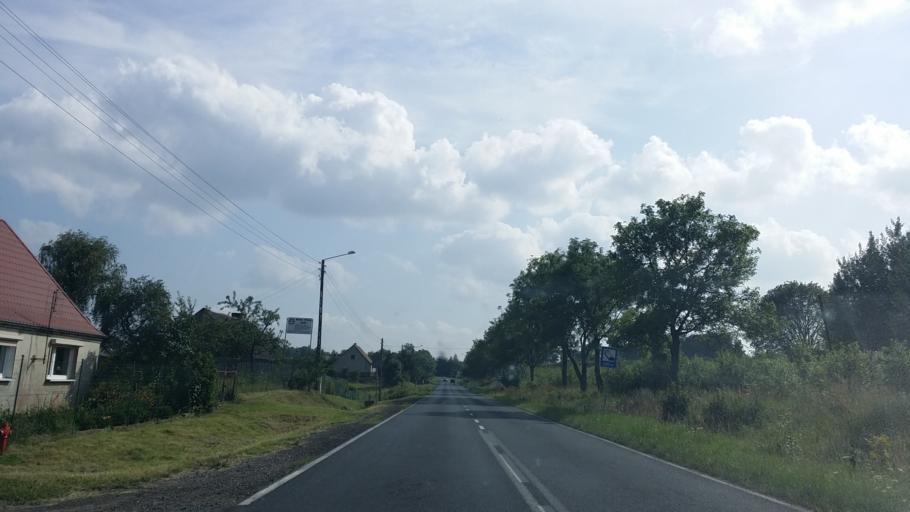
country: PL
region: West Pomeranian Voivodeship
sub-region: Powiat mysliborski
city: Barlinek
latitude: 52.9748
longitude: 15.1881
